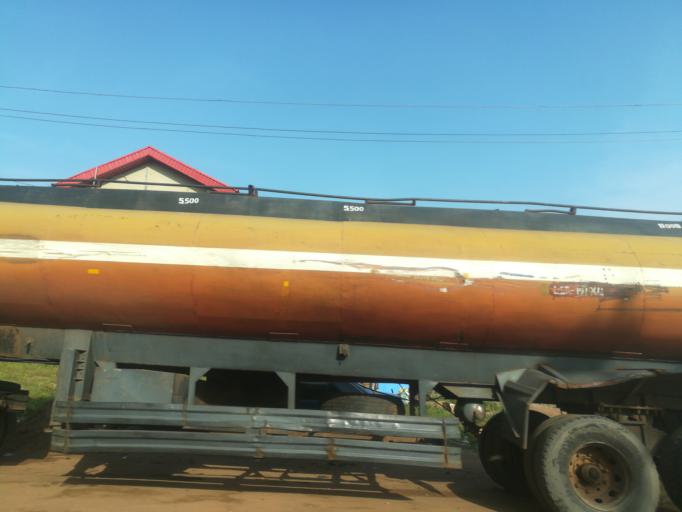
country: NG
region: Oyo
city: Moniya
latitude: 7.5223
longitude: 3.9120
